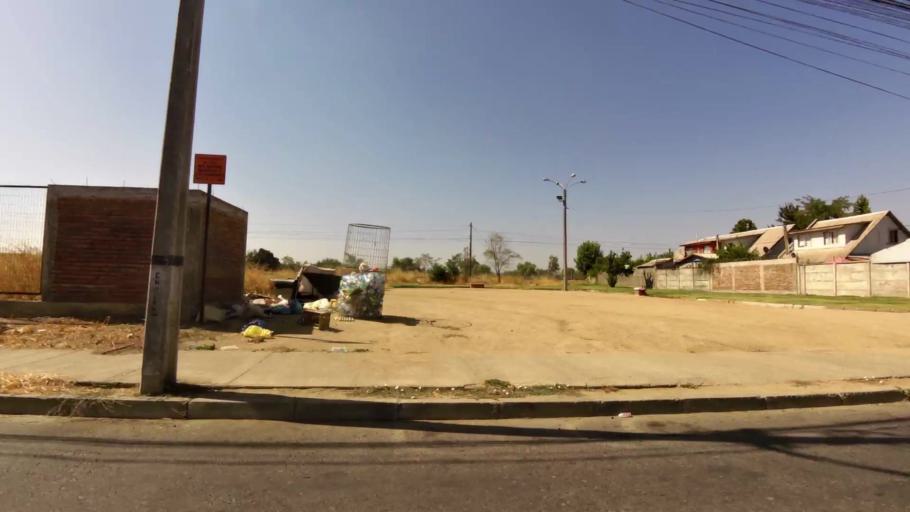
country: CL
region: Maule
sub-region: Provincia de Talca
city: Talca
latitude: -35.4106
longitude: -71.6360
